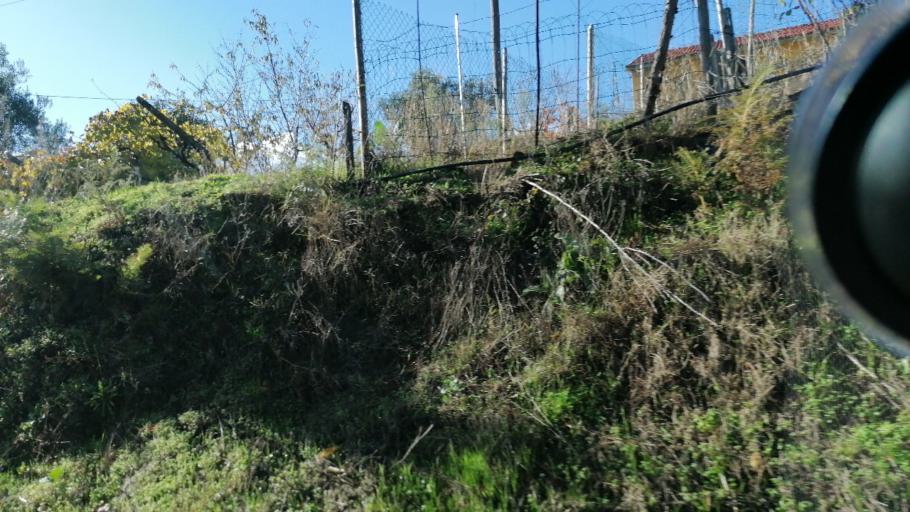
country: PT
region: Viseu
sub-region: Lamego
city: Lamego
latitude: 41.1059
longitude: -7.7936
